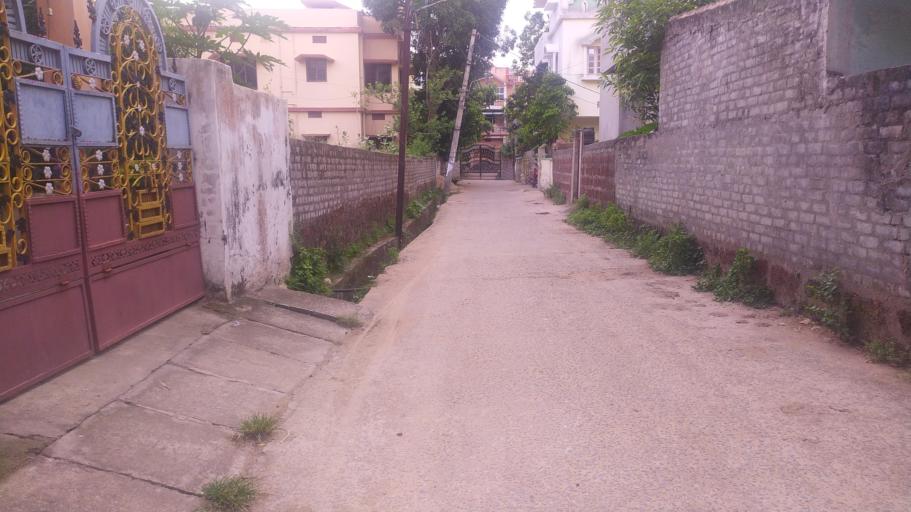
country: IN
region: Odisha
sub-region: Cuttack
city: Cuttack
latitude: 20.4902
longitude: 85.8424
